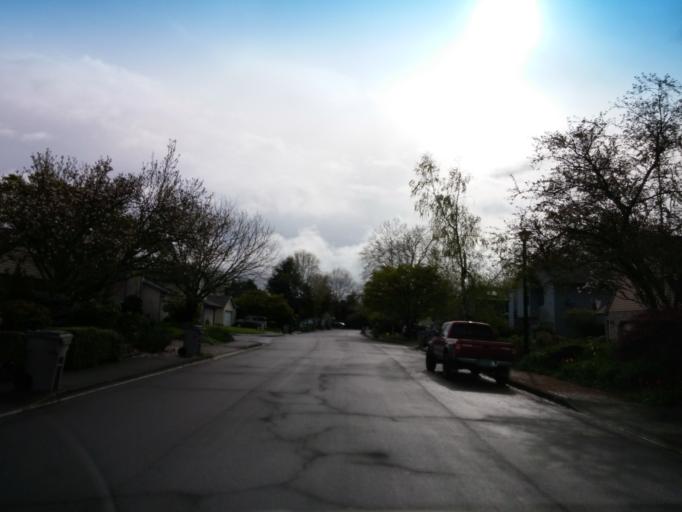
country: US
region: Oregon
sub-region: Washington County
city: Oak Hills
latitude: 45.5387
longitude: -122.8439
